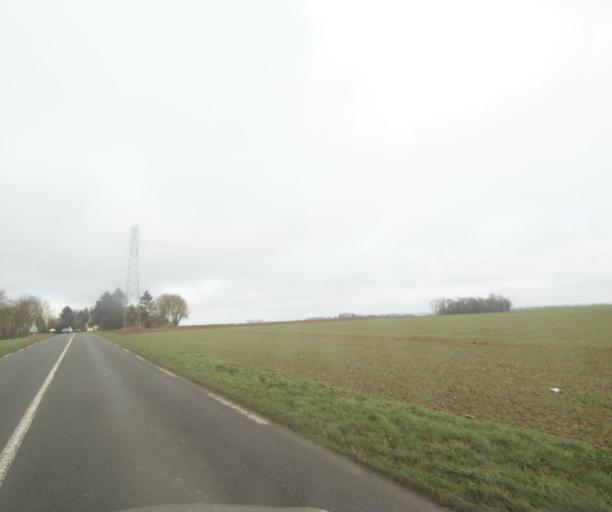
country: FR
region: Nord-Pas-de-Calais
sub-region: Departement du Nord
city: Vendegies-sur-Ecaillon
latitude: 50.2778
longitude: 3.5161
